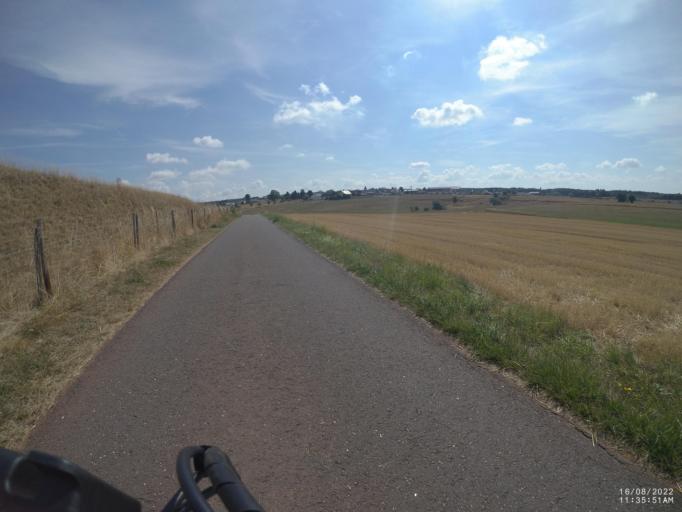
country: DE
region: Rheinland-Pfalz
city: Wiesbaum
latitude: 50.3418
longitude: 6.6606
